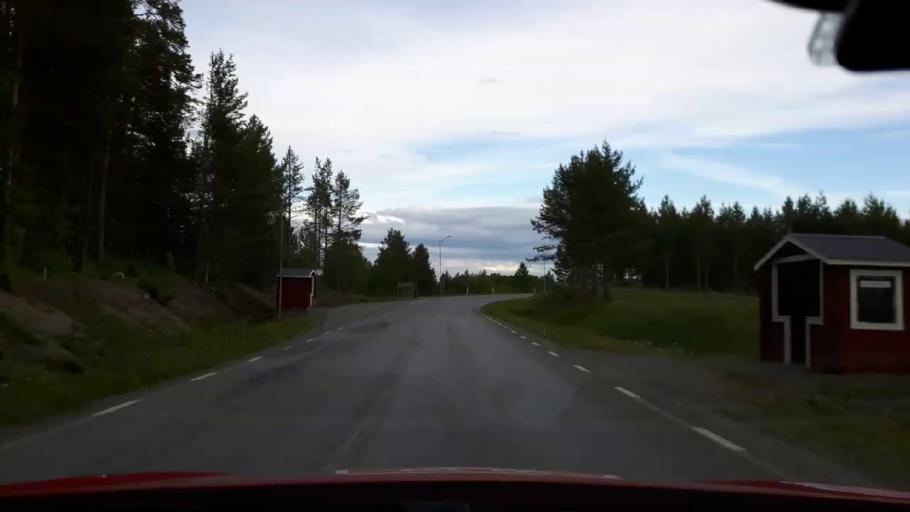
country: SE
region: Jaemtland
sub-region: Bergs Kommun
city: Hoverberg
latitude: 62.9767
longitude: 14.4831
